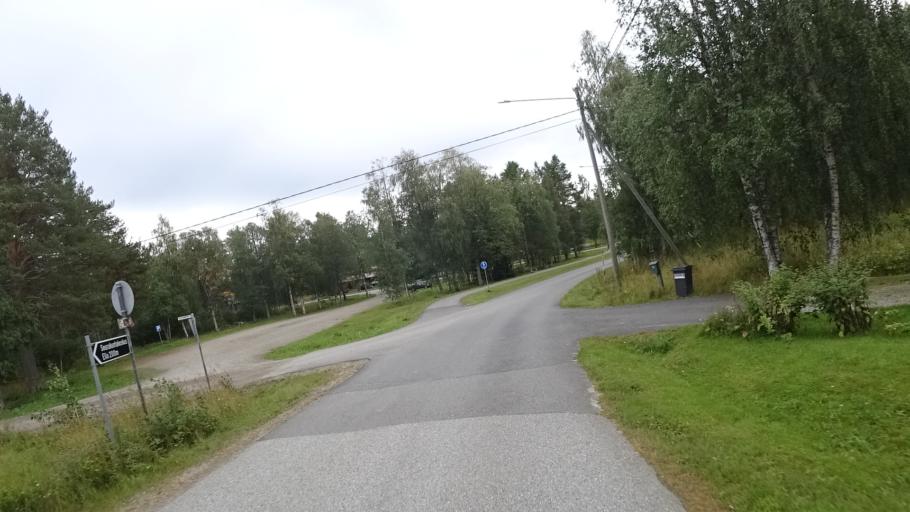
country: FI
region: North Karelia
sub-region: Joensuu
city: Ilomantsi
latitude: 62.6812
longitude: 30.9187
